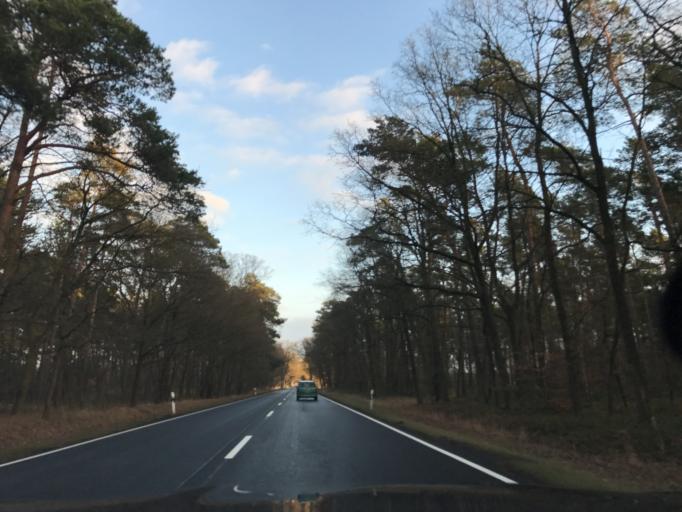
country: DE
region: Brandenburg
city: Bensdorf
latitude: 52.4111
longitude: 12.2938
